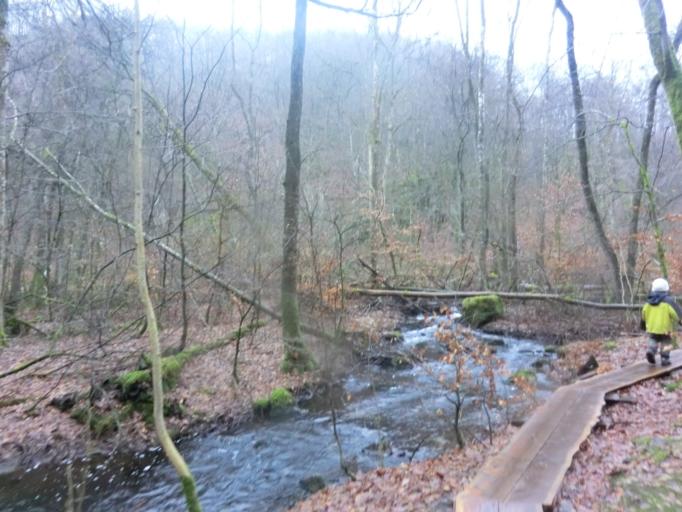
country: SE
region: Skane
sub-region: Klippans Kommun
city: Ljungbyhed
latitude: 56.0351
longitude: 13.2406
